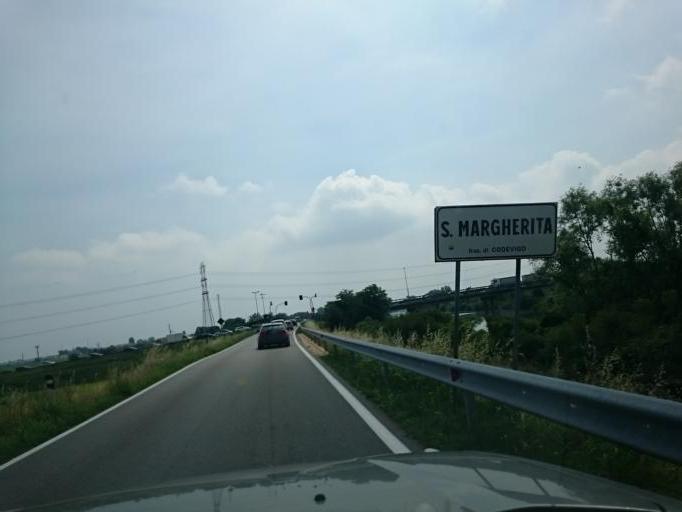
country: IT
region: Veneto
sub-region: Provincia di Padova
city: Codevigo
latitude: 45.2465
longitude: 12.1245
